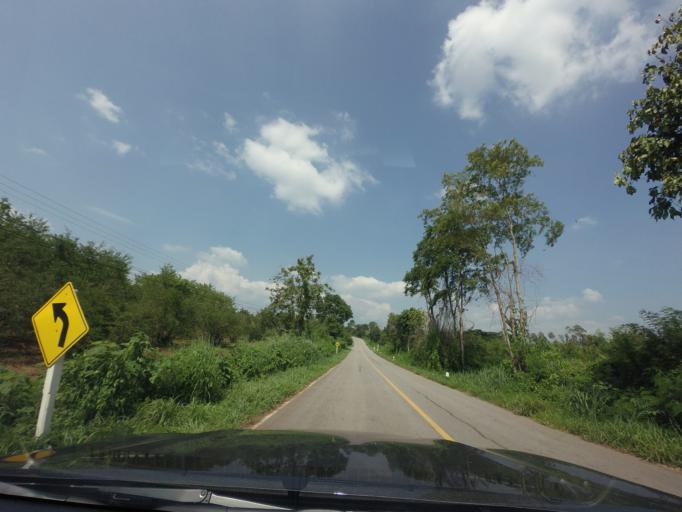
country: TH
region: Uttaradit
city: Ban Khok
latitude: 17.9634
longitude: 101.0179
